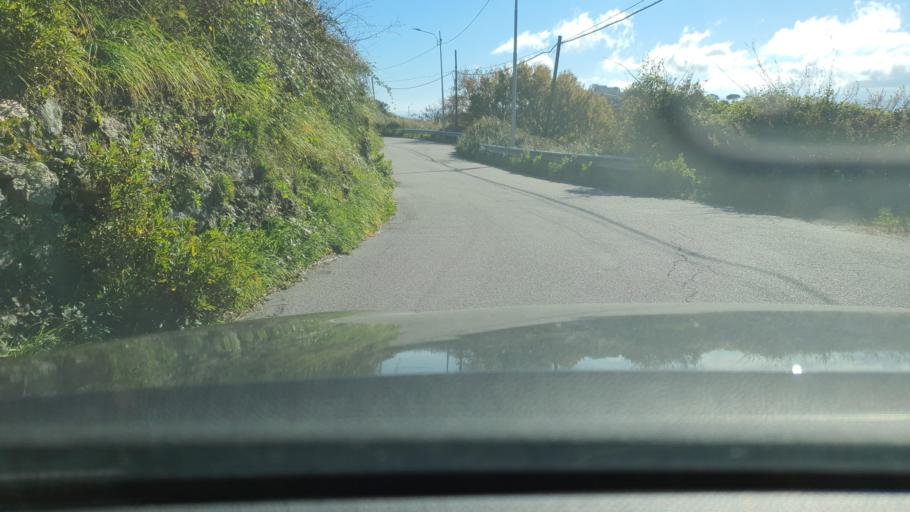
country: IT
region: Calabria
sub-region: Provincia di Catanzaro
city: Sant'Elia
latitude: 38.9521
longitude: 16.5810
